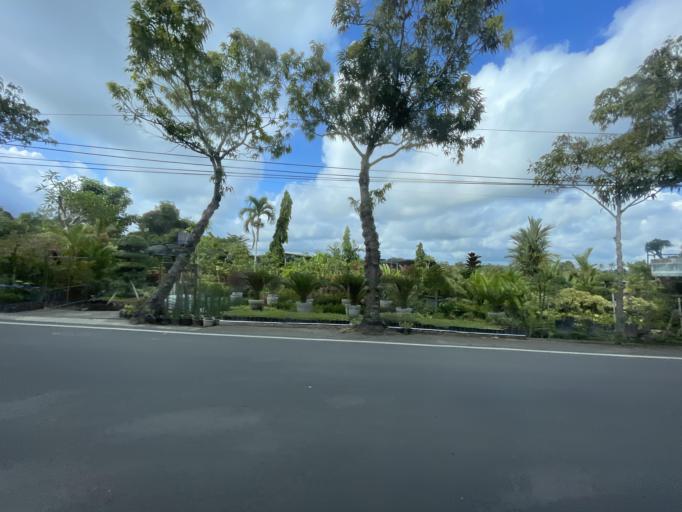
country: ID
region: Bali
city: Banjar Sedang
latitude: -8.5653
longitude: 115.2812
